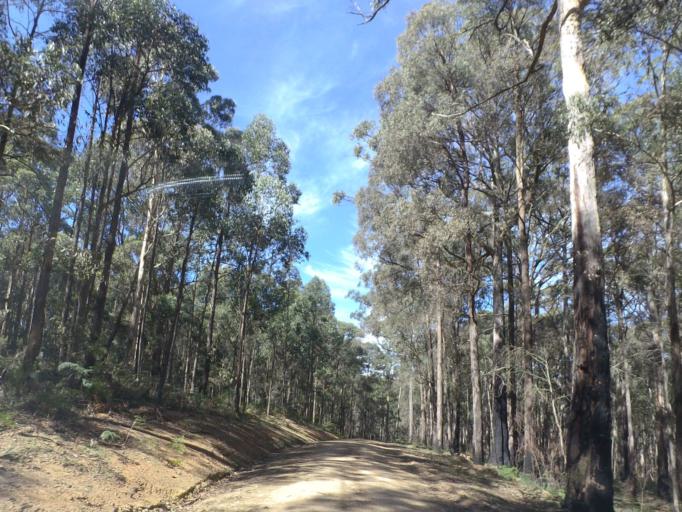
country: AU
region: Victoria
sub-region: Moorabool
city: Bacchus Marsh
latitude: -37.4218
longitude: 144.3405
